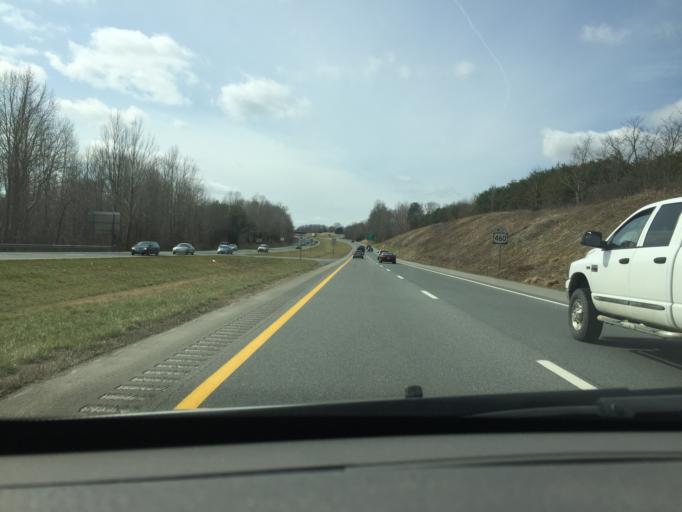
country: US
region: Virginia
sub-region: Campbell County
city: Timberlake
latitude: 37.3374
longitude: -79.2013
